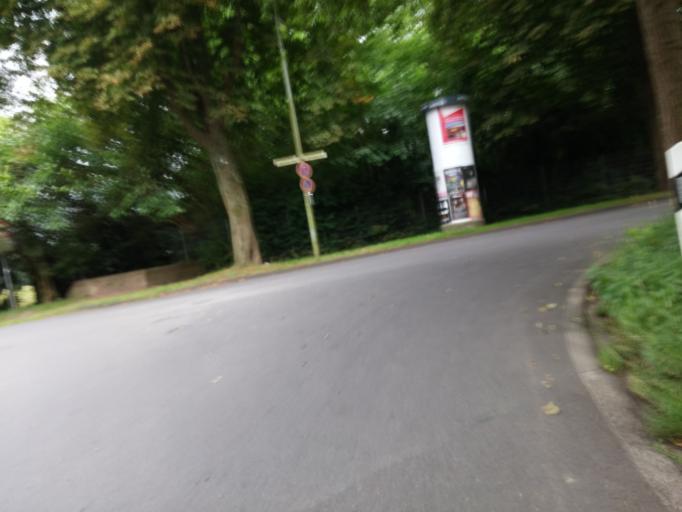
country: DE
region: North Rhine-Westphalia
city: Tonisvorst
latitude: 51.3762
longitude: 6.5176
